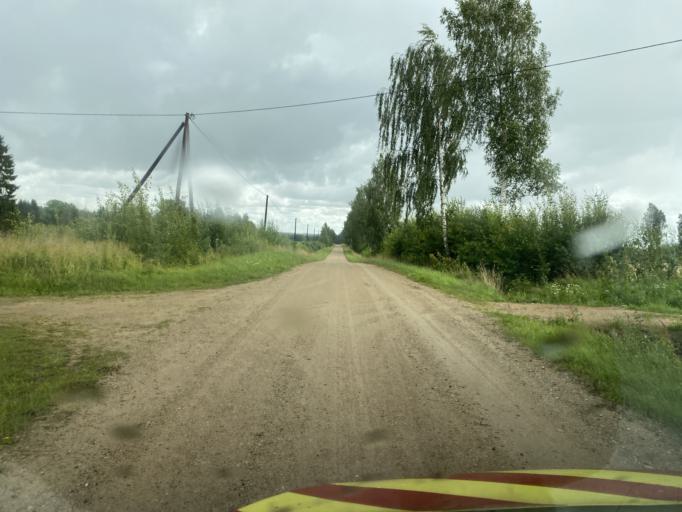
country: EE
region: Valgamaa
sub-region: Torva linn
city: Torva
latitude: 58.0951
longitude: 25.9374
